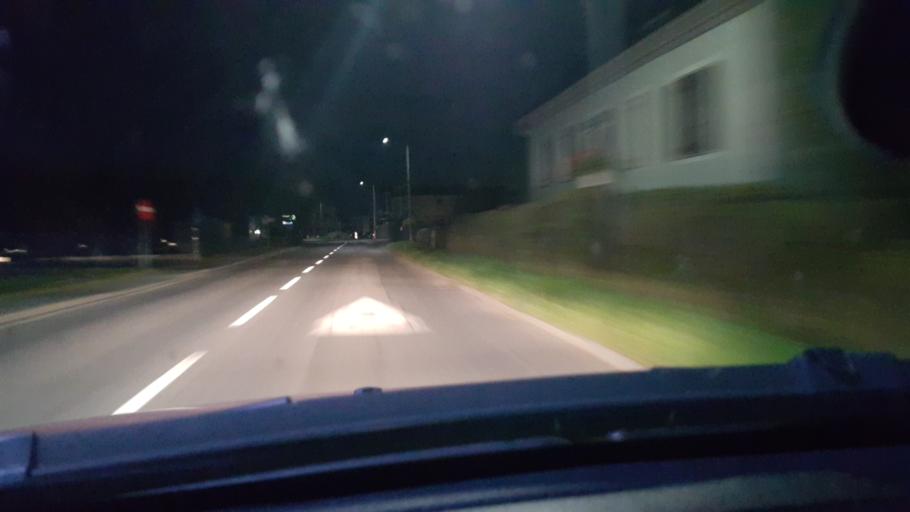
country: AT
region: Styria
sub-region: Politischer Bezirk Deutschlandsberg
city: Sankt Martin im Sulmtal
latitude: 46.7552
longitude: 15.2988
